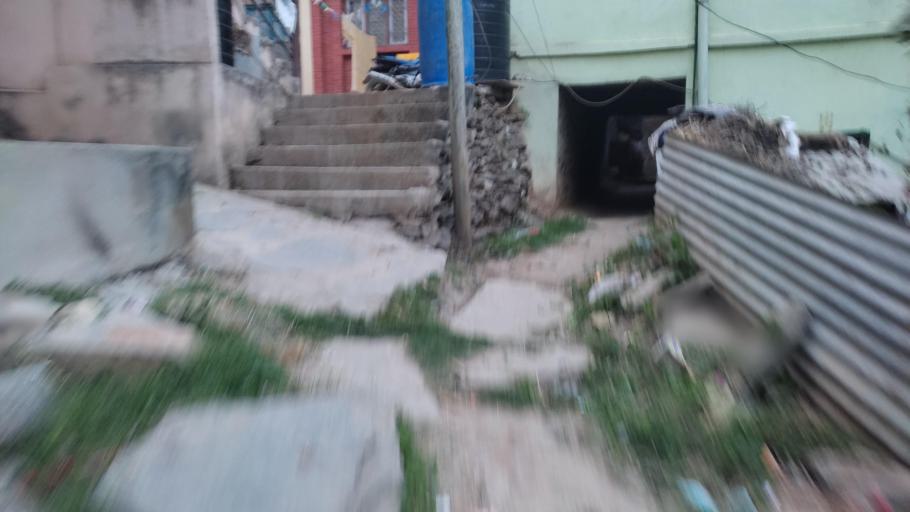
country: NP
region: Central Region
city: Kirtipur
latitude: 27.6715
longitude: 85.2853
